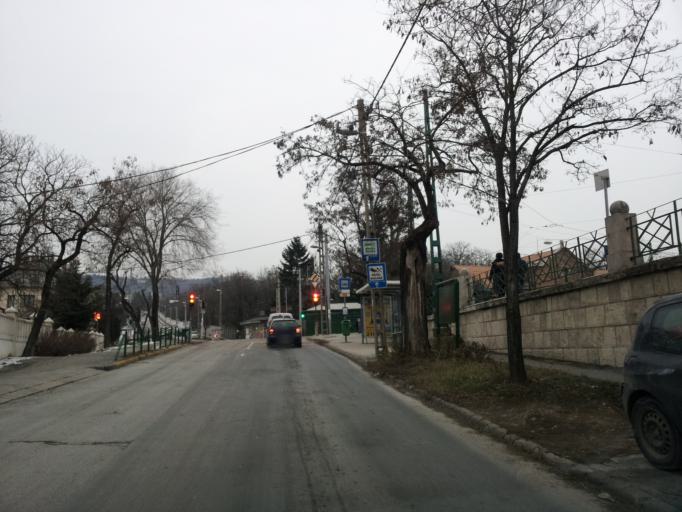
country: HU
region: Budapest
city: Budapest XII. keruelet
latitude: 47.4812
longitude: 18.9991
